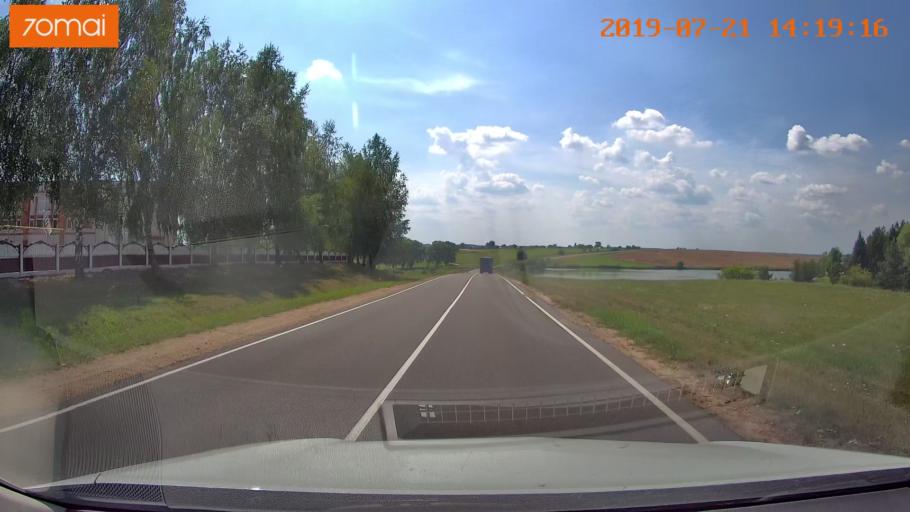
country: BY
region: Grodnenskaya
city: Karelichy
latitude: 53.5891
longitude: 26.1748
